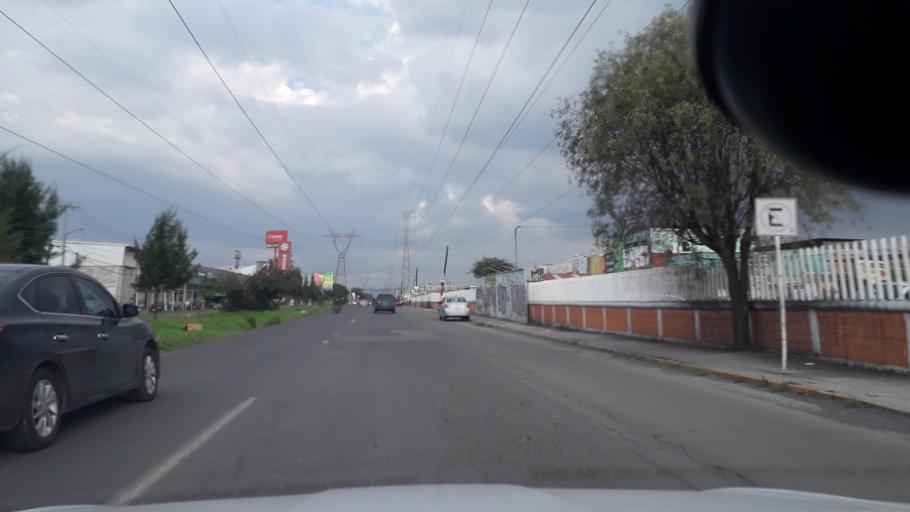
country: MX
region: Mexico
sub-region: Tultitlan
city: Fuentes del Valle
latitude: 19.6403
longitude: -99.1379
